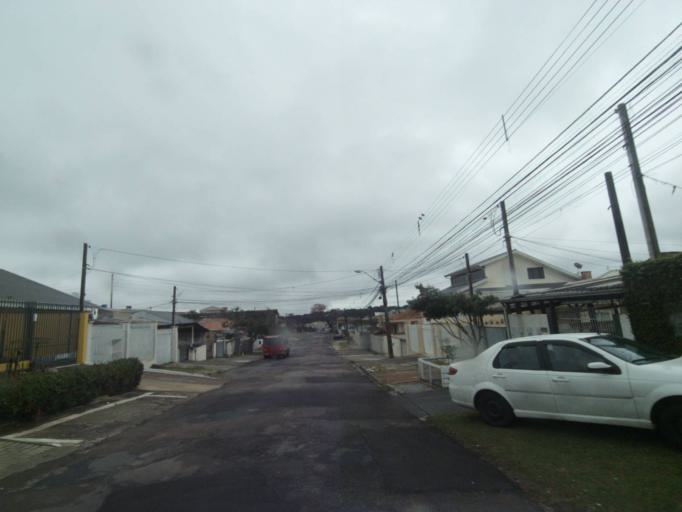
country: BR
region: Parana
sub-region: Curitiba
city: Curitiba
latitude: -25.5103
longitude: -49.3033
